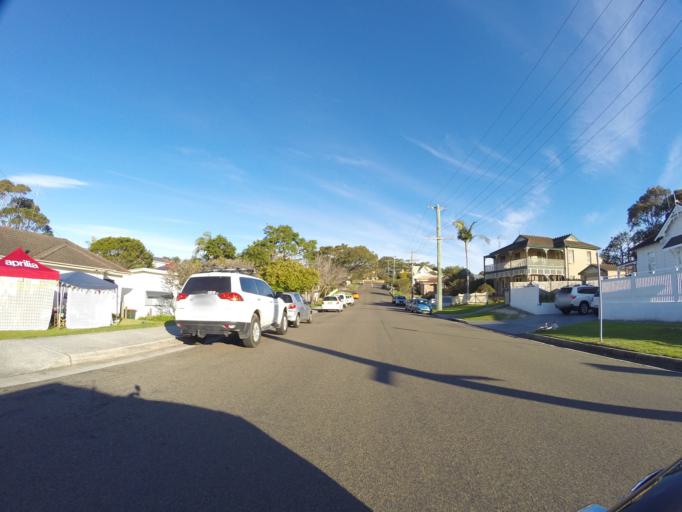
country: AU
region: New South Wales
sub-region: Wollongong
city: Bulli
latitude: -34.3186
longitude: 150.9233
